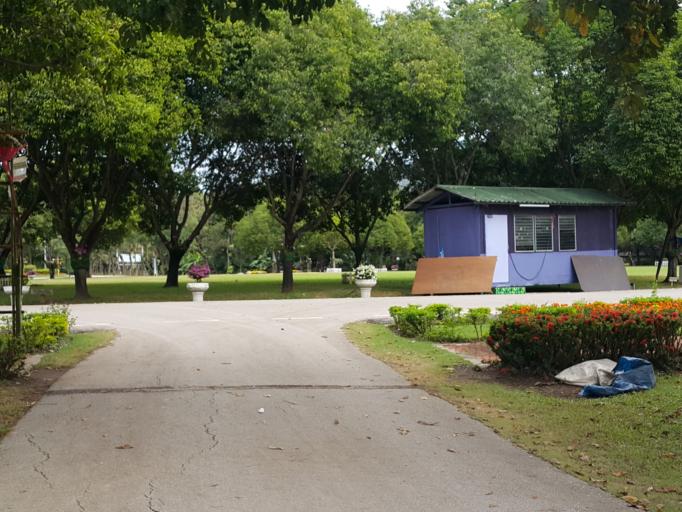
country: TH
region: Lampang
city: Mae Mo
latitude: 18.3160
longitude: 99.7412
